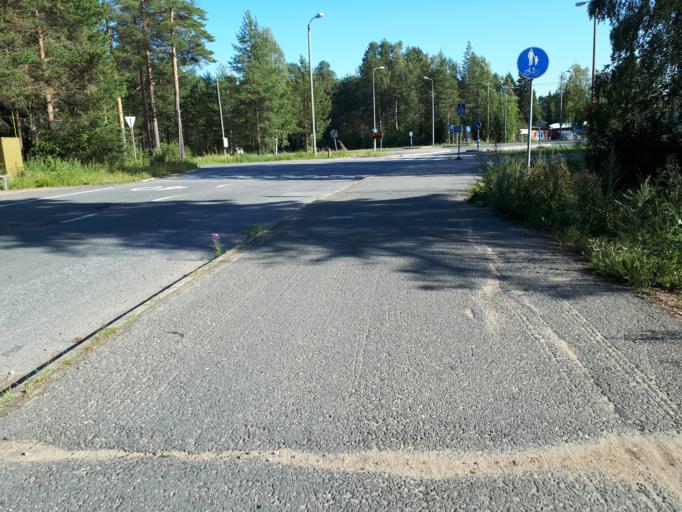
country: FI
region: Northern Ostrobothnia
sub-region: Oulunkaari
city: Ii
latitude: 65.3169
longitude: 25.3867
